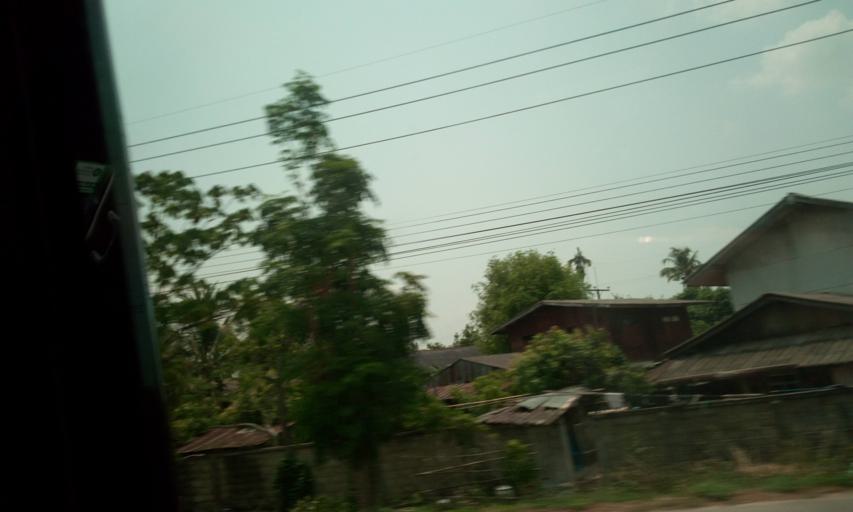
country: TH
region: Chiang Rai
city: Thoeng
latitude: 19.6750
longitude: 100.1174
